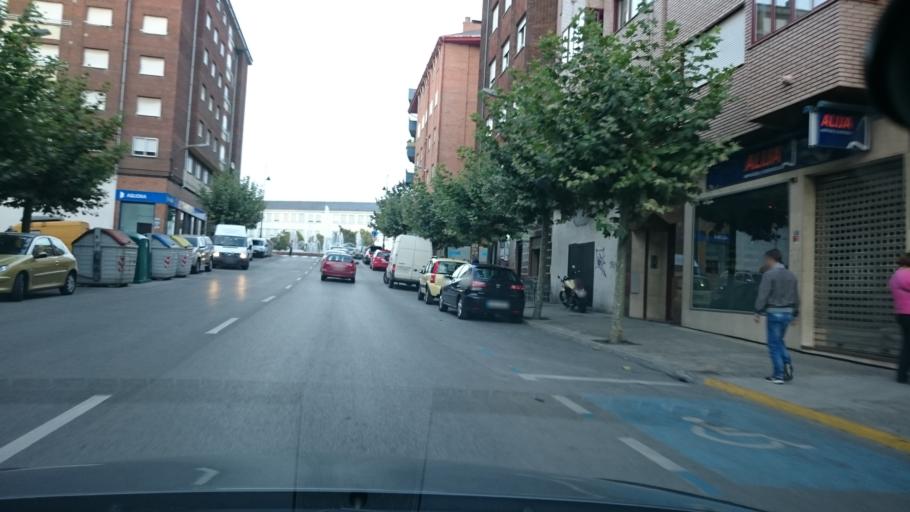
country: ES
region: Castille and Leon
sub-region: Provincia de Leon
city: Ponferrada
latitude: 42.5442
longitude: -6.5977
